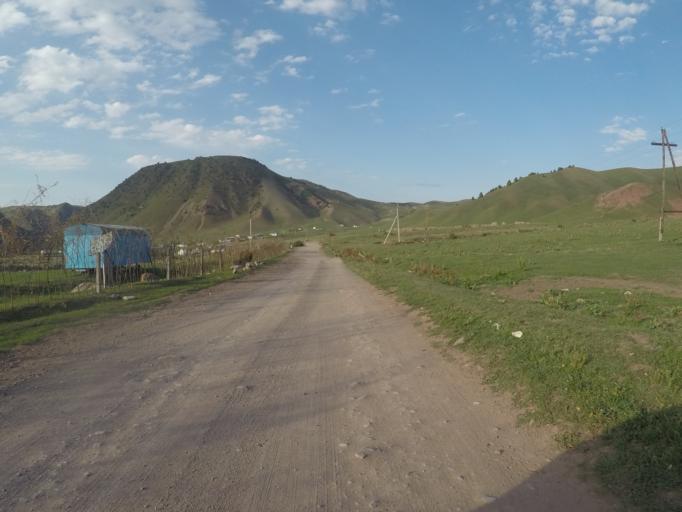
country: KG
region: Chuy
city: Bishkek
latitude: 42.6362
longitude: 74.6178
